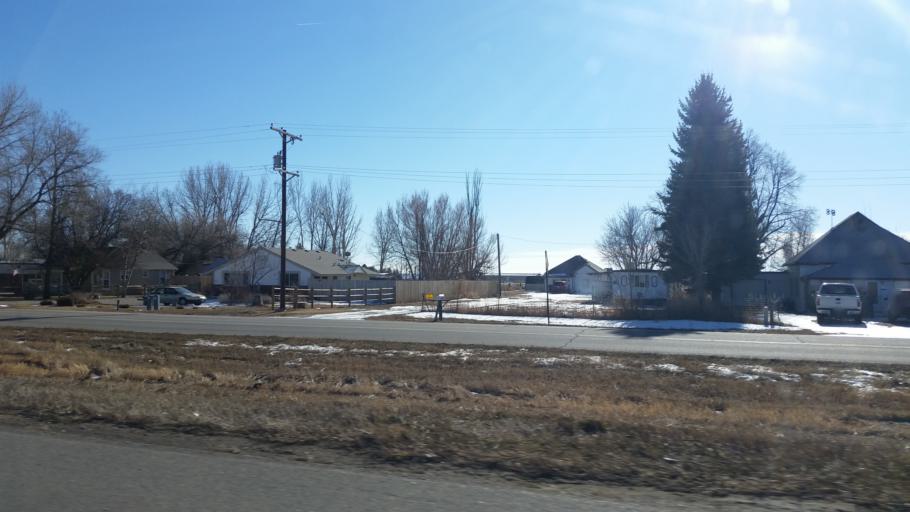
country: US
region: Colorado
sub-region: Weld County
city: Johnstown
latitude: 40.4072
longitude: -104.9531
